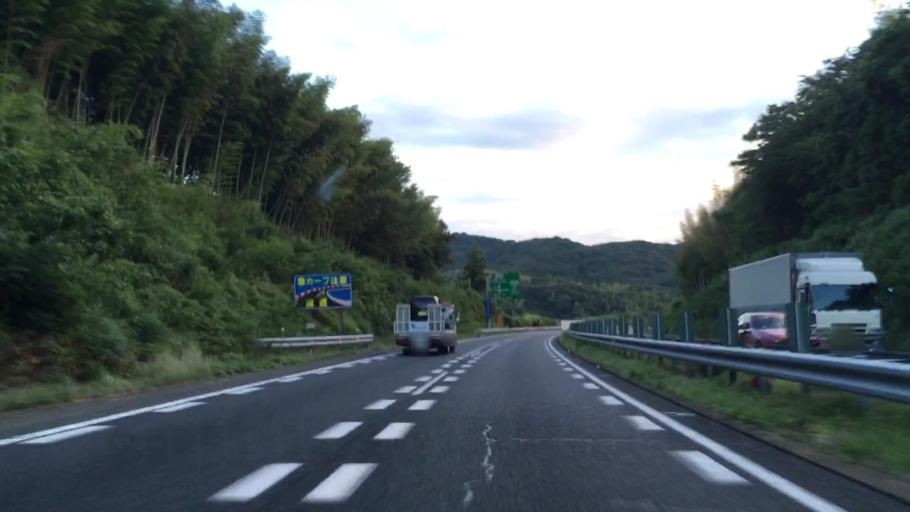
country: JP
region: Yamaguchi
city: Shimonoseki
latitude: 33.9328
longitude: 130.9958
